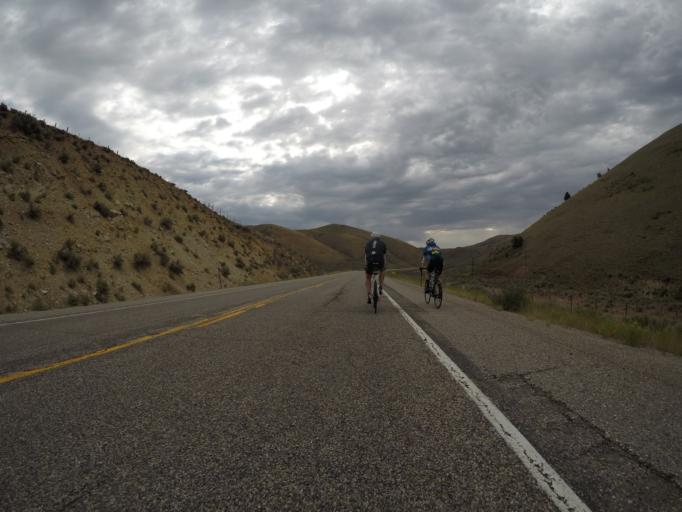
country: US
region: Wyoming
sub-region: Lincoln County
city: Kemmerer
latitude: 41.8251
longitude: -110.8456
